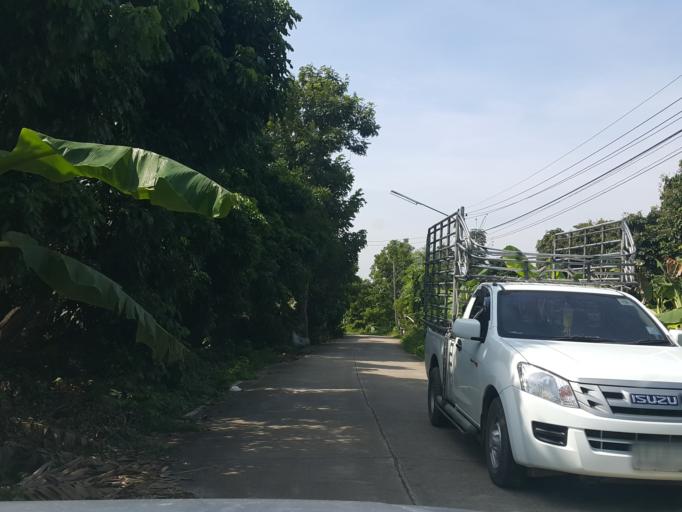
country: TH
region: Chiang Mai
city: Saraphi
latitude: 18.6906
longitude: 99.0700
